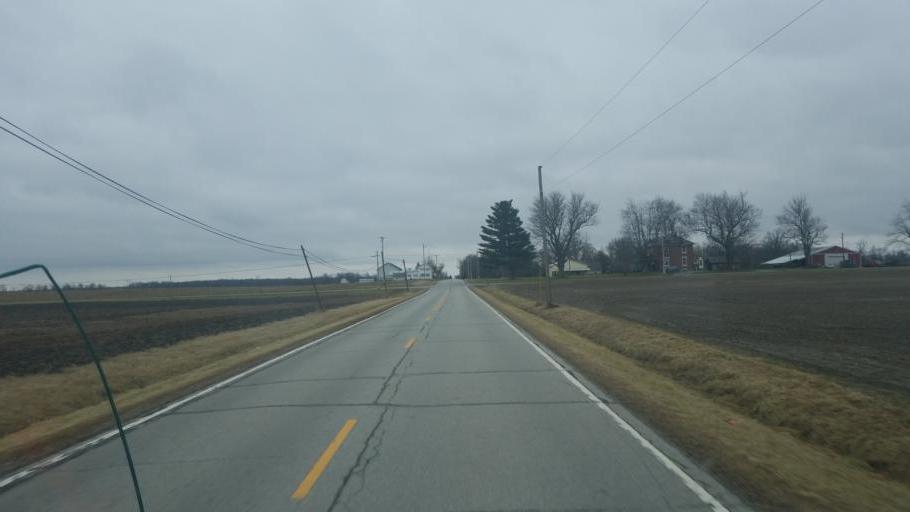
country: US
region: Ohio
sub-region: Crawford County
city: Bucyrus
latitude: 40.7627
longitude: -82.9539
